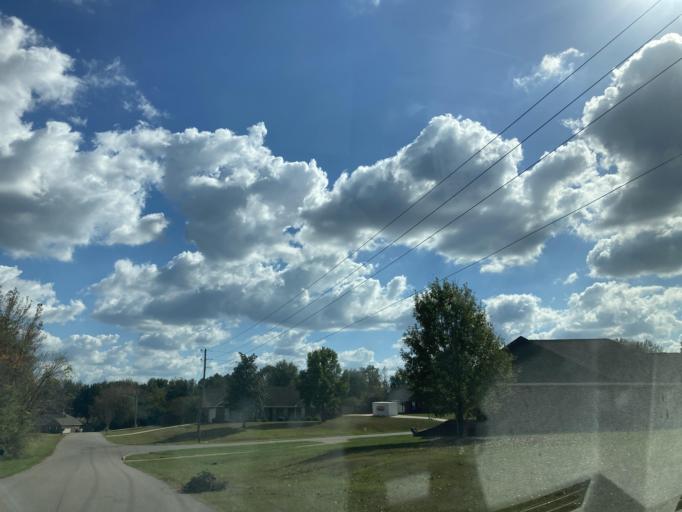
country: US
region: Mississippi
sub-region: Lamar County
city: Sumrall
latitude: 31.3958
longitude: -89.5388
